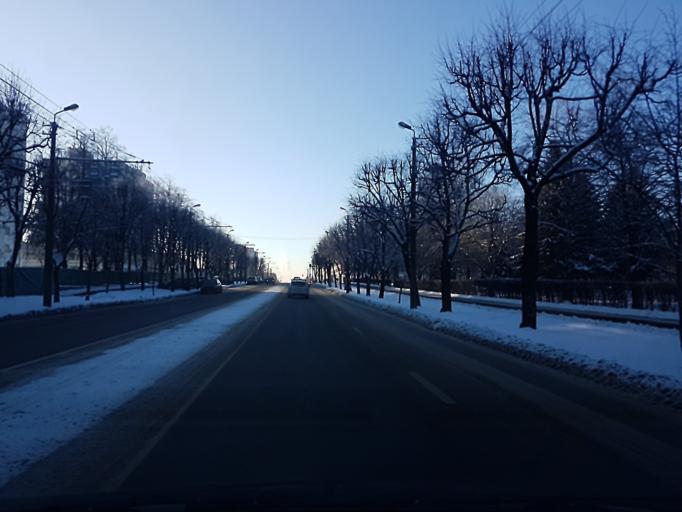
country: BY
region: Minsk
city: Minsk
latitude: 53.8939
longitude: 27.5176
